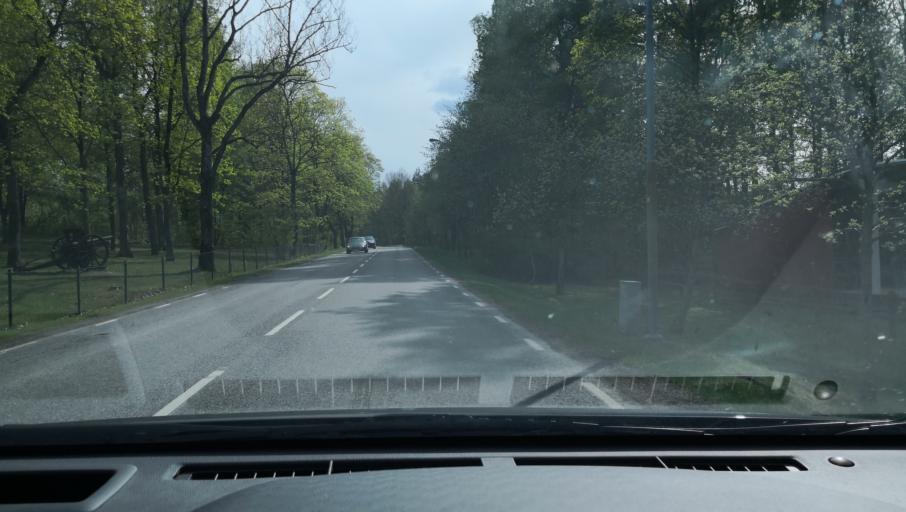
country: SE
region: OErebro
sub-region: Kumla Kommun
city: Kumla
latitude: 59.0947
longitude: 15.1602
